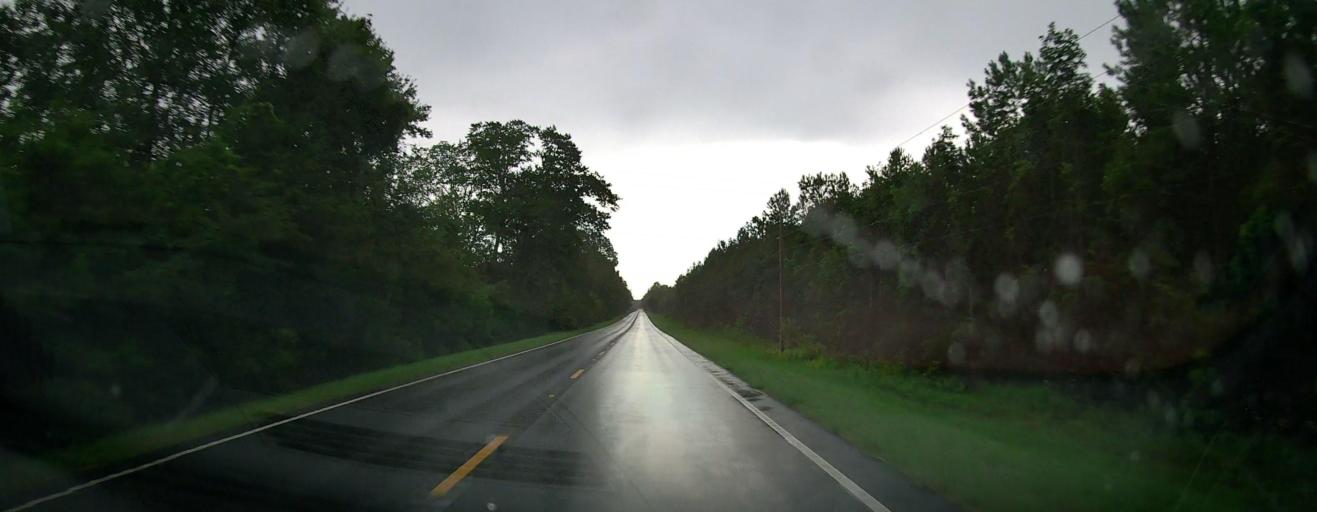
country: US
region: Georgia
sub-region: Glynn County
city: Dock Junction
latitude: 31.3073
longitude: -81.7233
